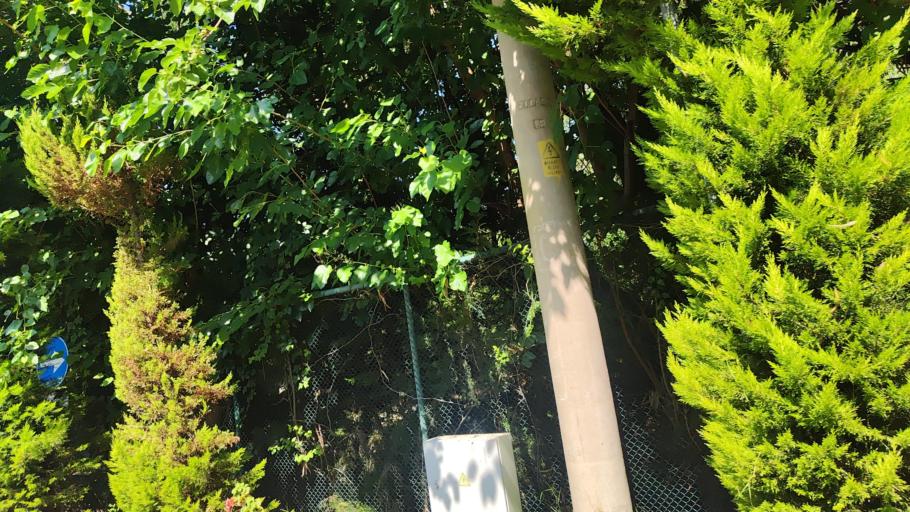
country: TR
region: Mugla
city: Sarigerme
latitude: 36.7022
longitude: 28.6950
